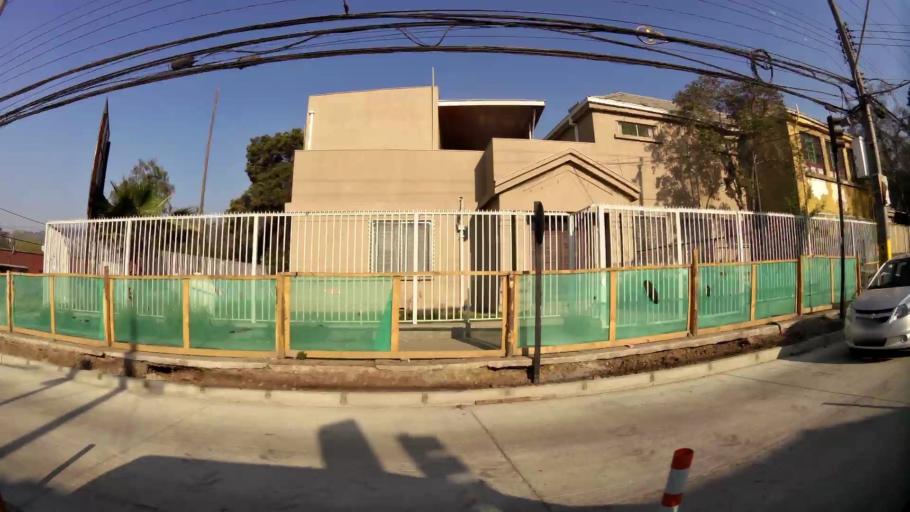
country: CL
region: Santiago Metropolitan
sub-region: Provincia de Santiago
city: Santiago
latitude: -33.4014
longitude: -70.6301
